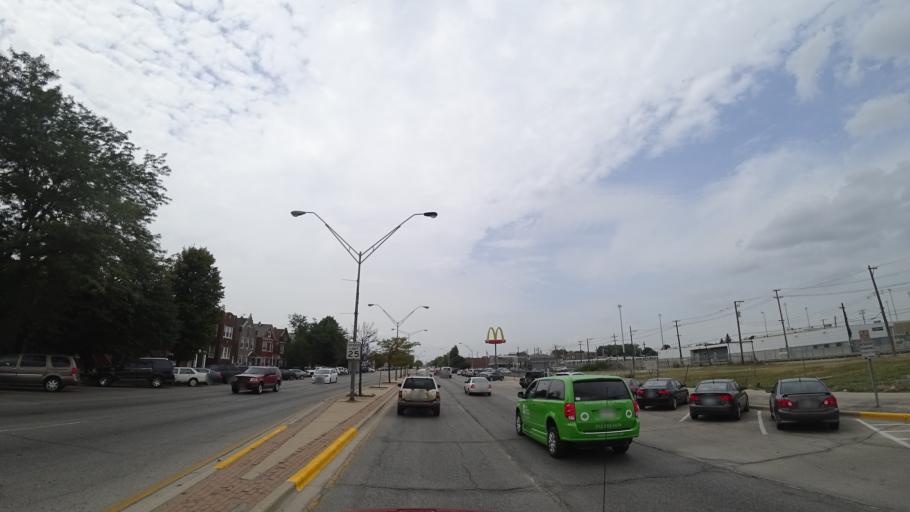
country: US
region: Illinois
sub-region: Cook County
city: Cicero
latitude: 41.8511
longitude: -87.7596
